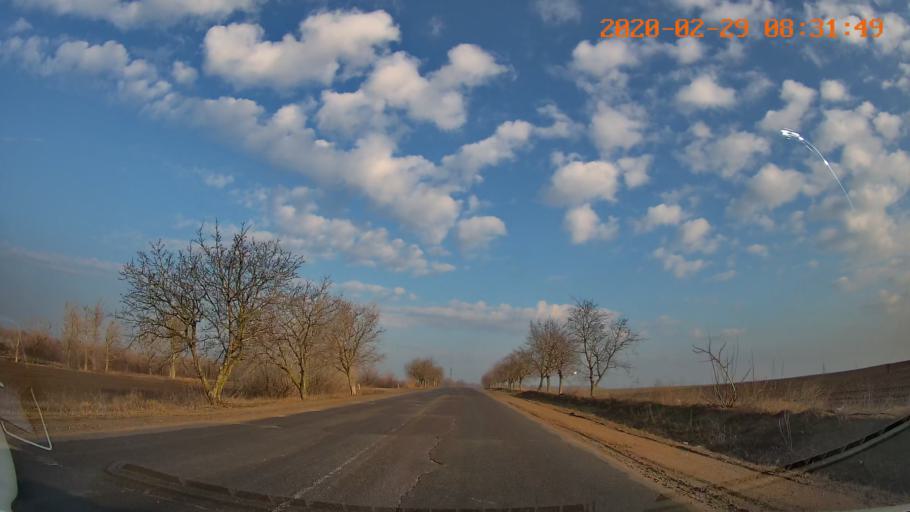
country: MD
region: Anenii Noi
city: Anenii Noi
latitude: 46.9174
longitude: 29.2880
